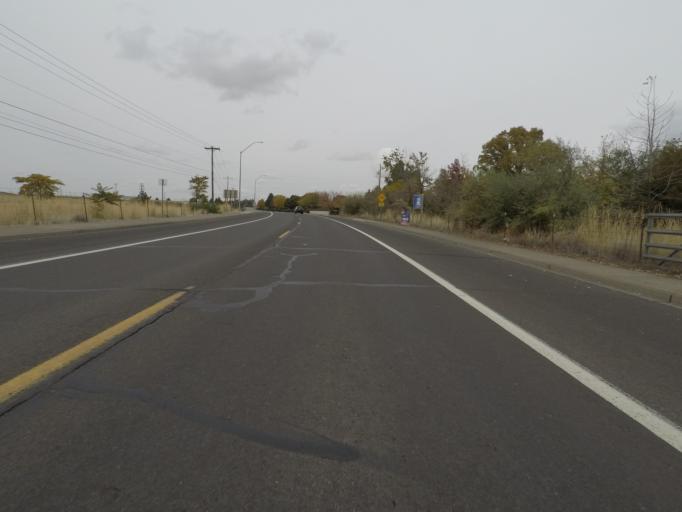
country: US
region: Washington
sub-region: Walla Walla County
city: Walla Walla East
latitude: 46.0754
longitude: -118.2841
